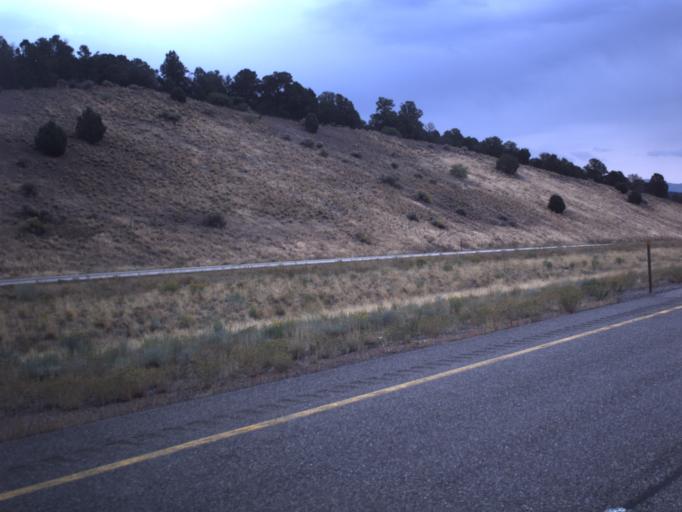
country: US
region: Utah
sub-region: Beaver County
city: Beaver
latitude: 38.5784
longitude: -112.4778
